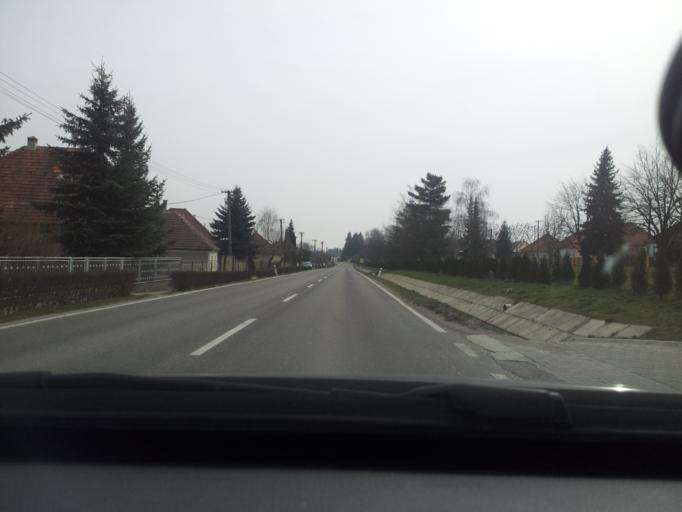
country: SK
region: Trnavsky
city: Hlohovec
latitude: 48.3717
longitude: 17.8892
